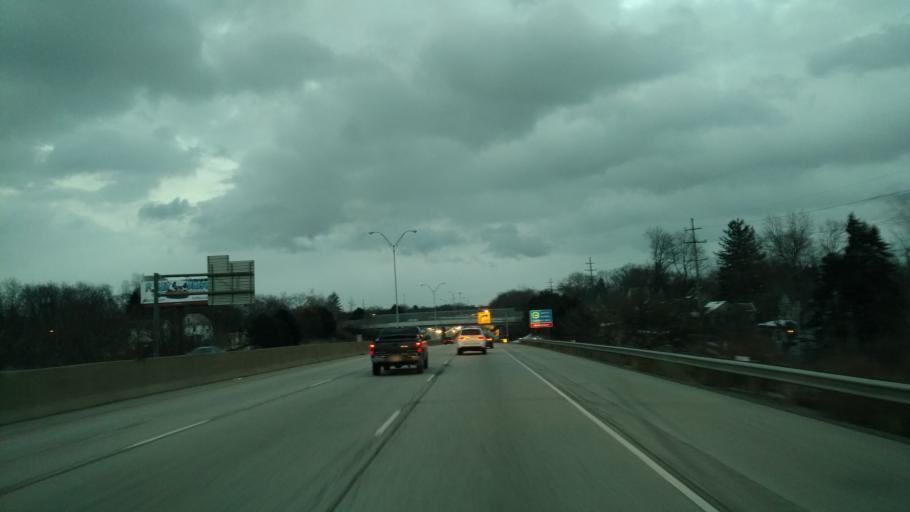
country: US
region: Ohio
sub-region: Summit County
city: Barberton
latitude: 41.0355
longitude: -81.5745
